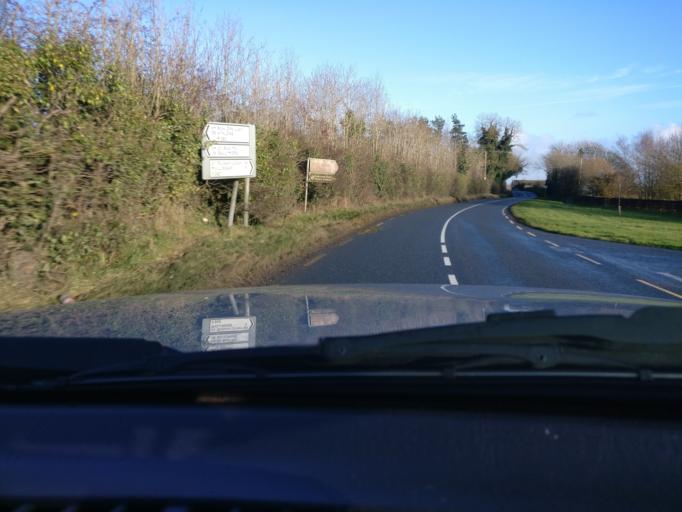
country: IE
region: Leinster
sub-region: An Iarmhi
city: An Muileann gCearr
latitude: 53.5107
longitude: -7.4078
